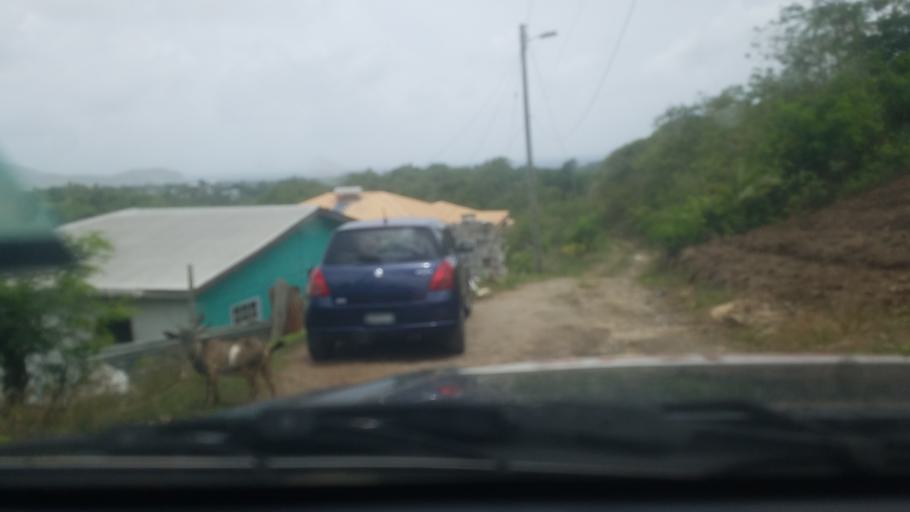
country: LC
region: Laborie Quarter
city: Laborie
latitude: 13.7569
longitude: -60.9855
